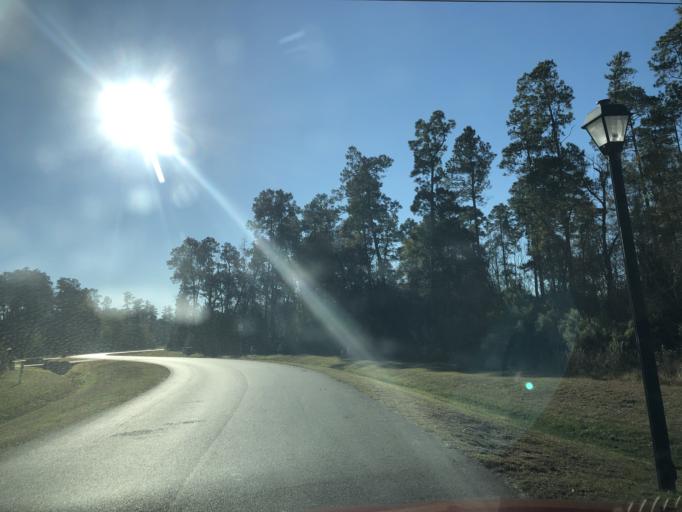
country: US
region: Texas
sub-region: Montgomery County
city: Porter Heights
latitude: 30.0805
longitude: -95.3223
